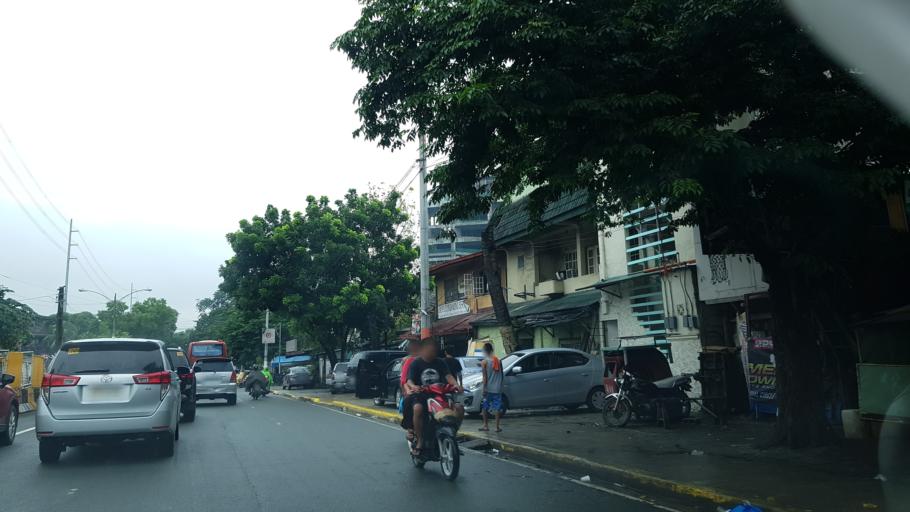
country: PH
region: Metro Manila
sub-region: City of Manila
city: Quiapo
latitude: 14.5756
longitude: 120.9957
